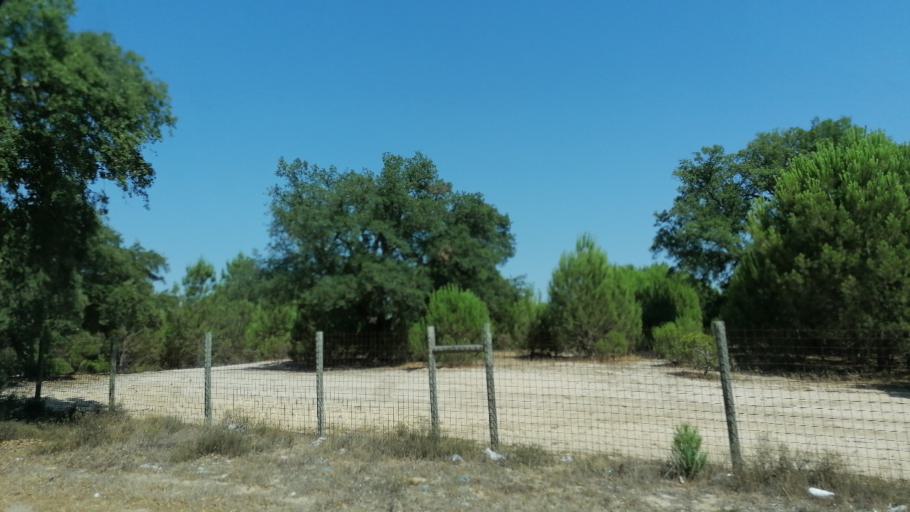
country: PT
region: Santarem
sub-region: Benavente
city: Poceirao
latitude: 38.7249
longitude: -8.7059
